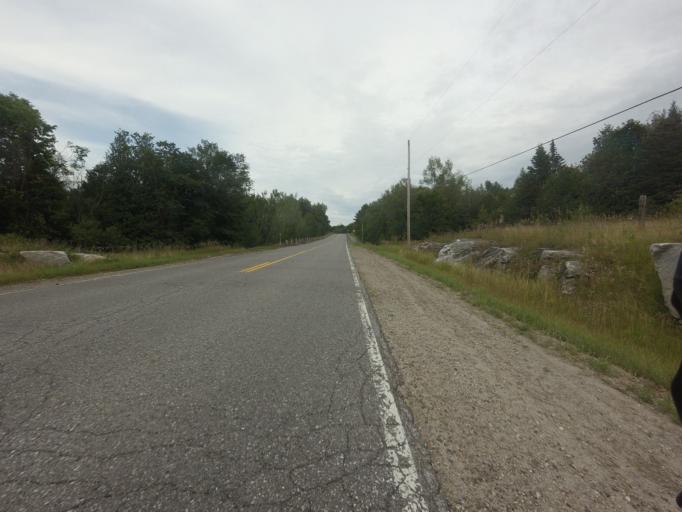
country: CA
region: Ontario
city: Carleton Place
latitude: 45.1127
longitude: -76.3614
